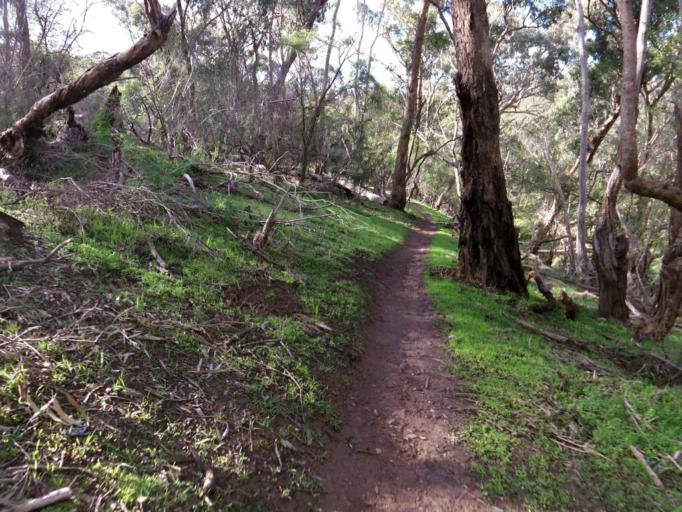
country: AU
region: Victoria
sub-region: Banyule
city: Watsonia North
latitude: -37.6823
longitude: 145.0863
